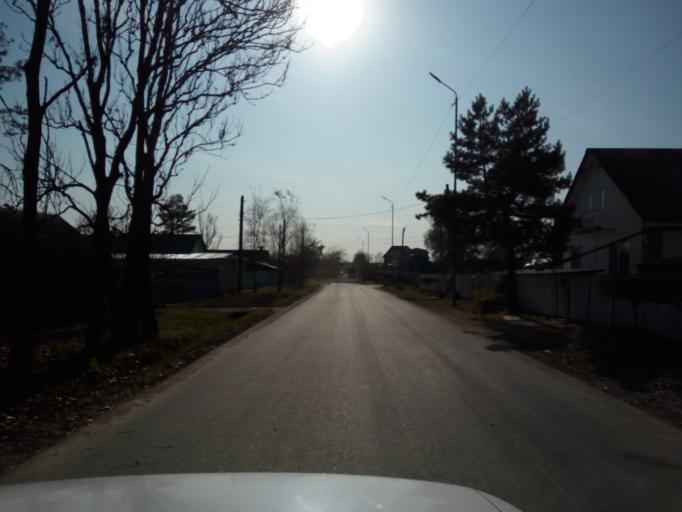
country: RU
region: Primorskiy
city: Dal'nerechensk
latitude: 45.9230
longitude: 133.7273
